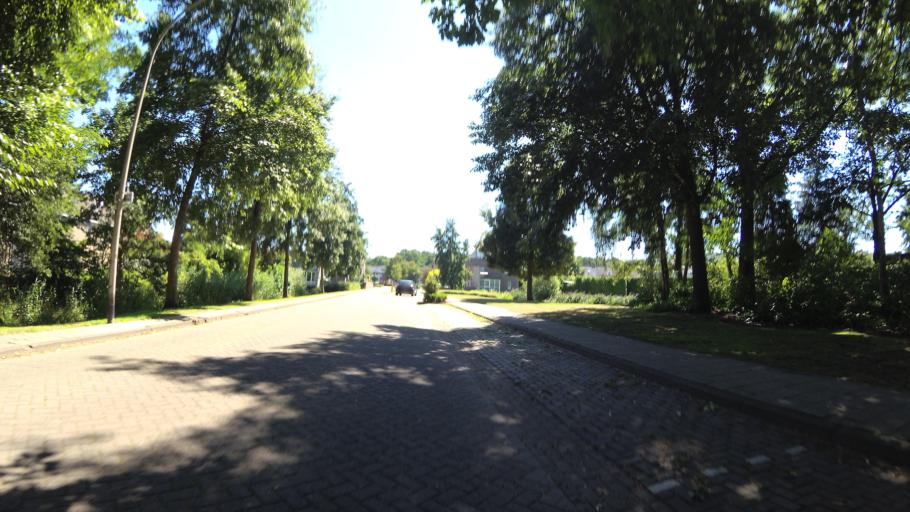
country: NL
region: North Brabant
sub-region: Gemeente Waalwijk
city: Waalwijk
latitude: 51.6734
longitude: 5.0674
